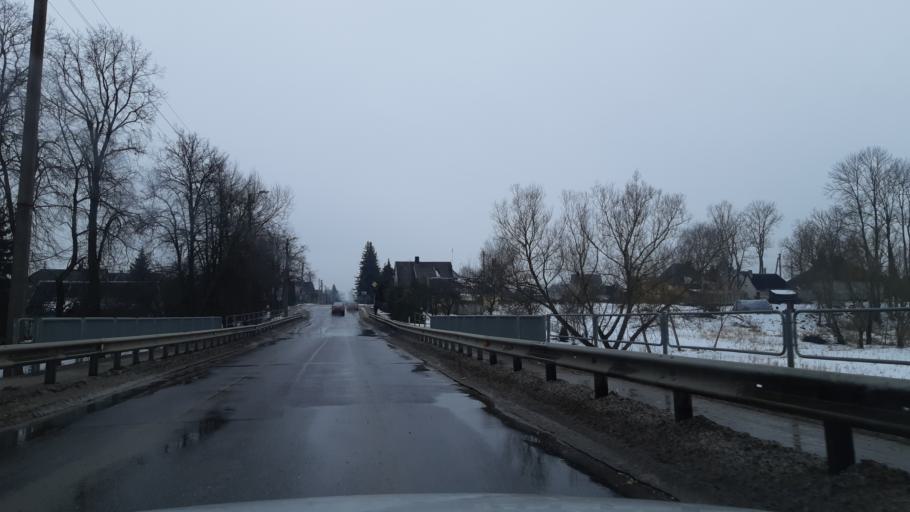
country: LT
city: Vilkaviskis
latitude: 54.6501
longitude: 23.0239
